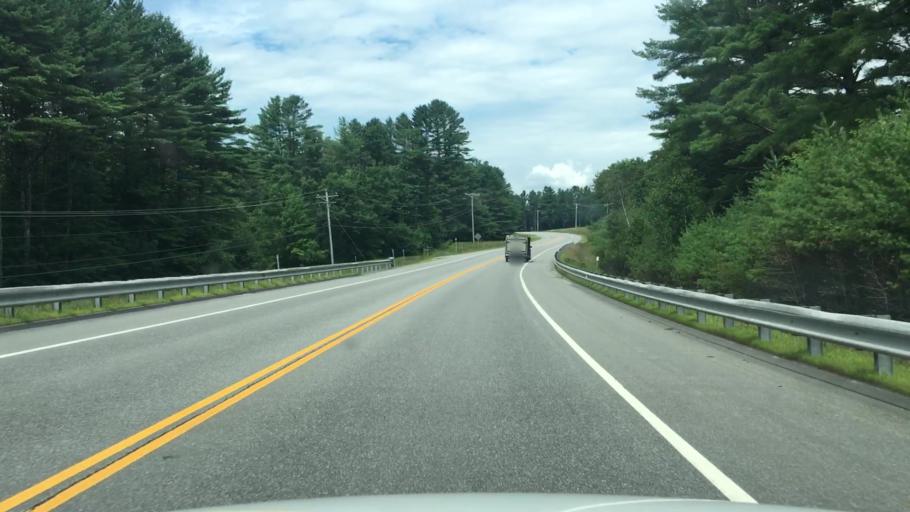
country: US
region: New Hampshire
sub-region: Grafton County
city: Rumney
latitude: 43.8245
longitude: -71.8927
